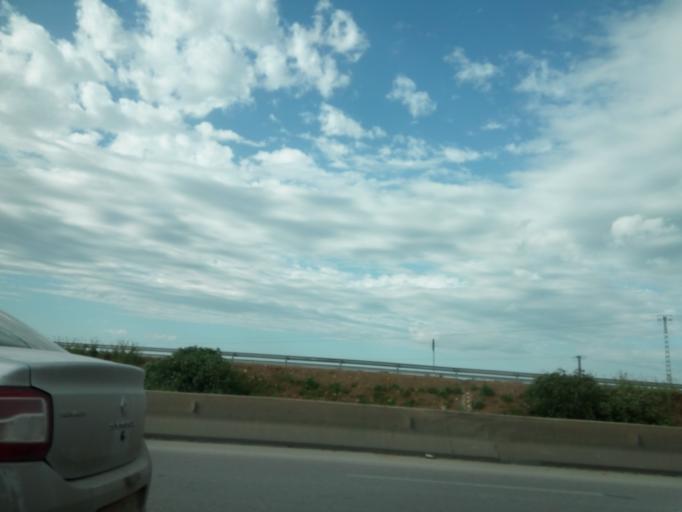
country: DZ
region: Tipaza
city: Mouzaia
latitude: 36.4496
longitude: 2.6909
